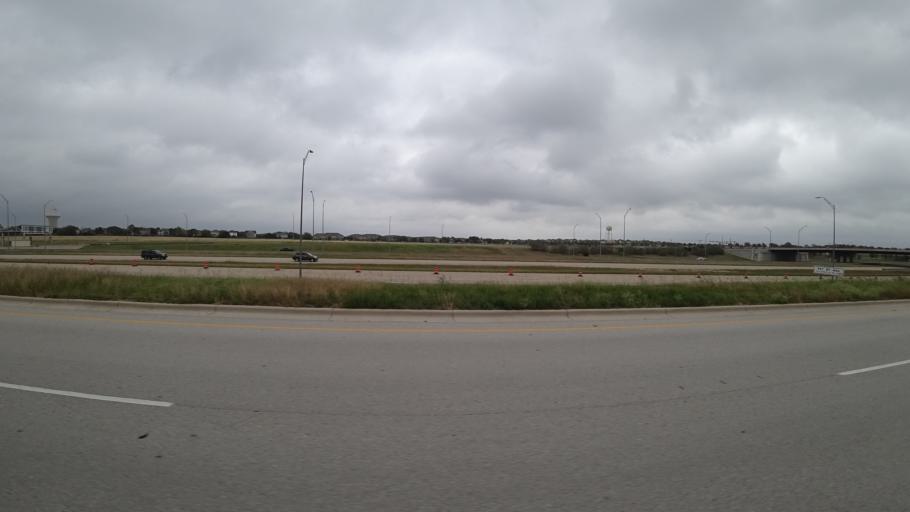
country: US
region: Texas
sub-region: Travis County
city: Windemere
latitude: 30.4841
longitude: -97.6165
